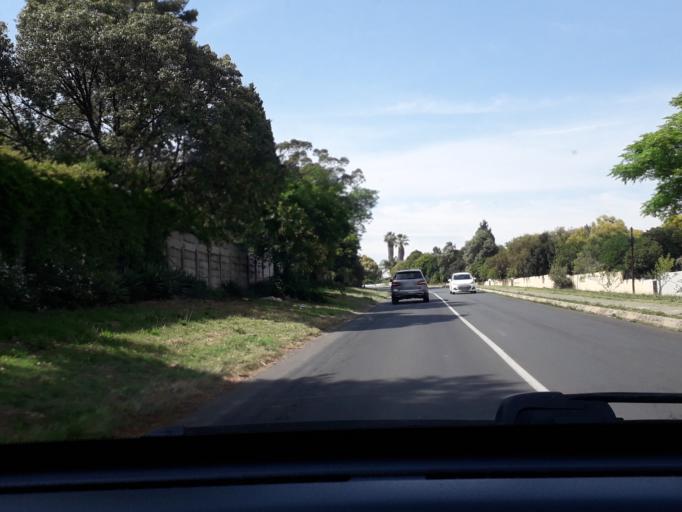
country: ZA
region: Gauteng
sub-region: City of Johannesburg Metropolitan Municipality
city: Midrand
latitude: -26.0459
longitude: 28.0517
